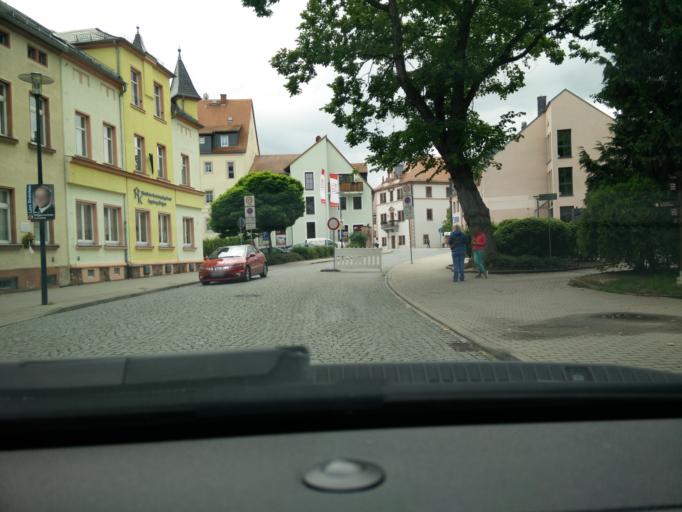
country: DE
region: Saxony
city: Geithain
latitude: 51.0552
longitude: 12.6953
